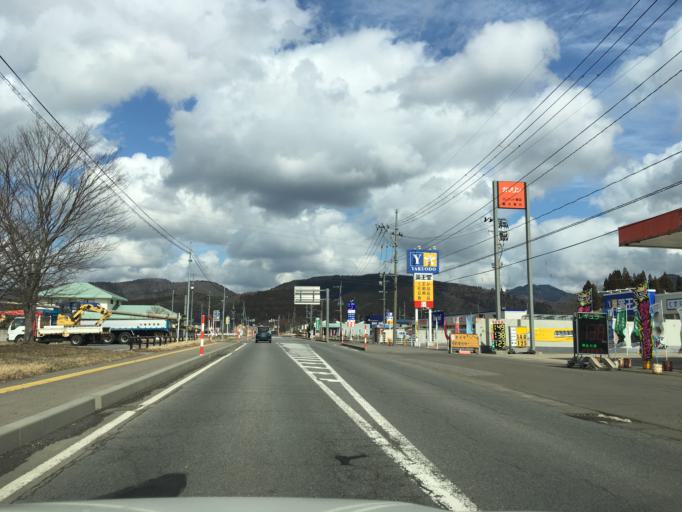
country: JP
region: Akita
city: Odate
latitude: 40.2196
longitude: 140.5863
